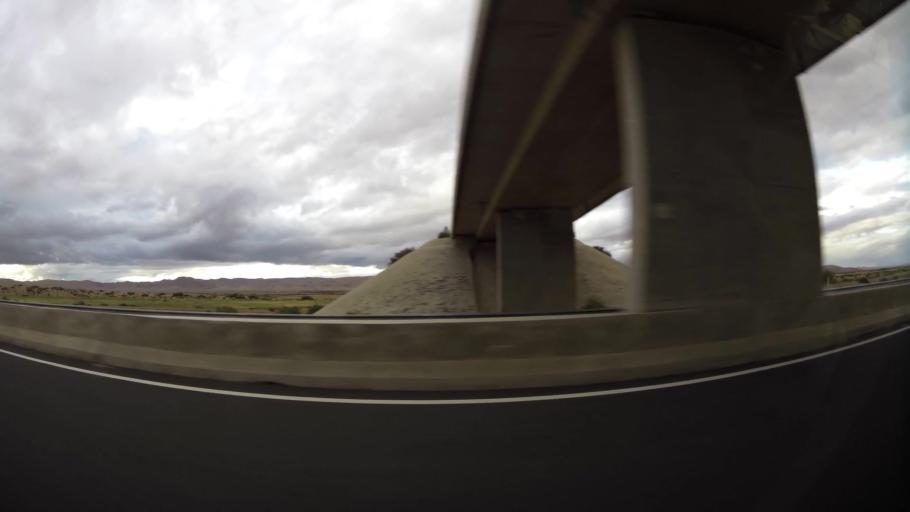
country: MA
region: Taza-Al Hoceima-Taounate
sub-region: Taza
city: Guercif
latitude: 34.3048
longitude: -3.6281
